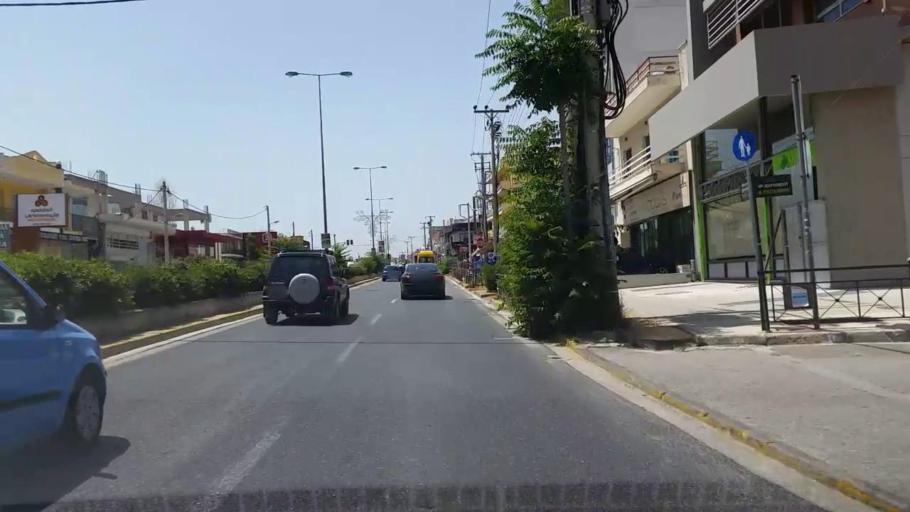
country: GR
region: Attica
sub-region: Nomarchia Anatolikis Attikis
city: Gerakas
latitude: 38.0079
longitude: 23.8575
